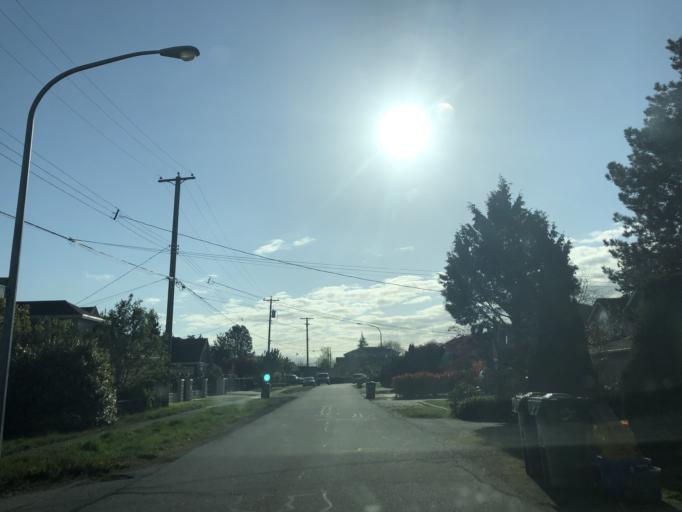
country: CA
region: British Columbia
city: Richmond
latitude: 49.1440
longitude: -123.1172
